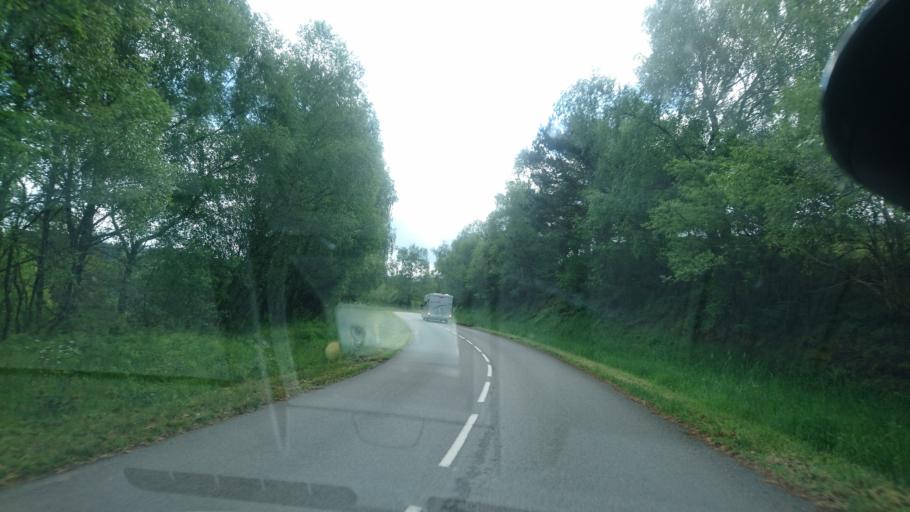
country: FR
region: Limousin
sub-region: Departement de la Haute-Vienne
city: Peyrat-le-Chateau
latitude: 45.7812
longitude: 1.8476
